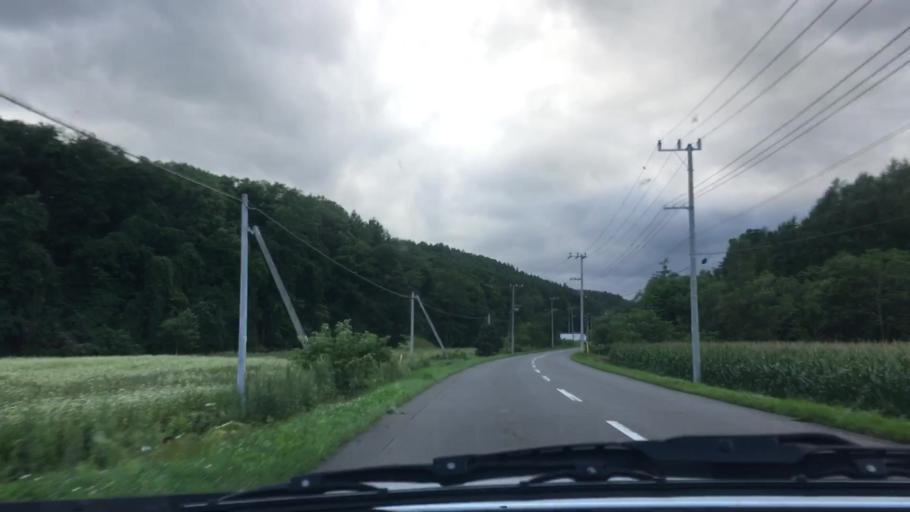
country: JP
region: Hokkaido
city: Otofuke
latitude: 43.1417
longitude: 142.8848
